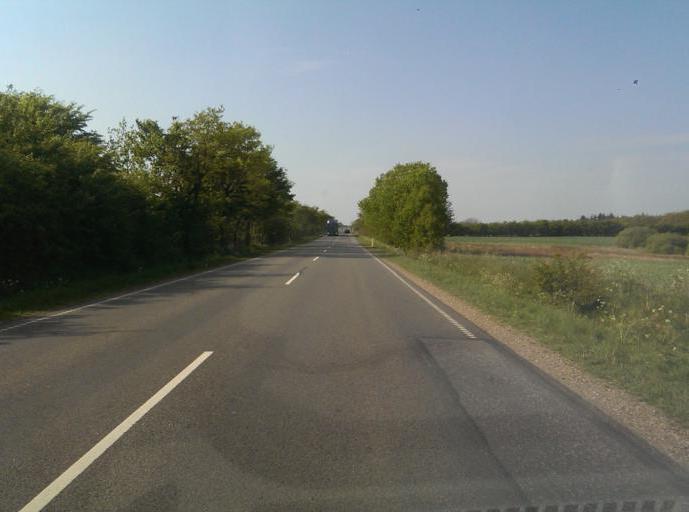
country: DK
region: South Denmark
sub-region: Esbjerg Kommune
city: Tjaereborg
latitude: 55.5100
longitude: 8.5958
